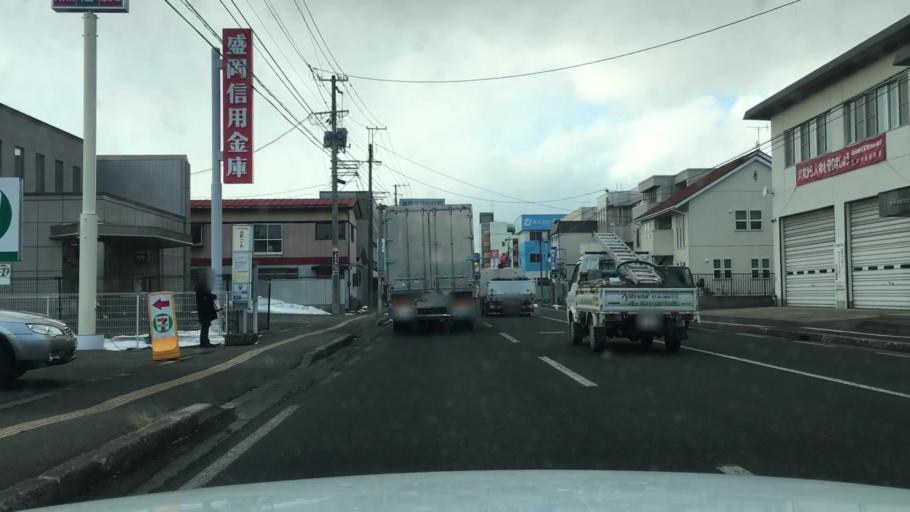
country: JP
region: Iwate
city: Morioka-shi
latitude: 39.6928
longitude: 141.1710
